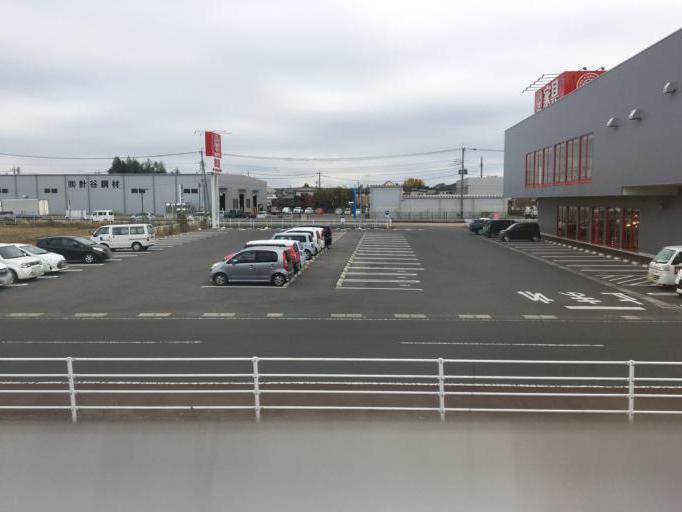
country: JP
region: Tochigi
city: Tochigi
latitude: 36.3467
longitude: 139.7015
